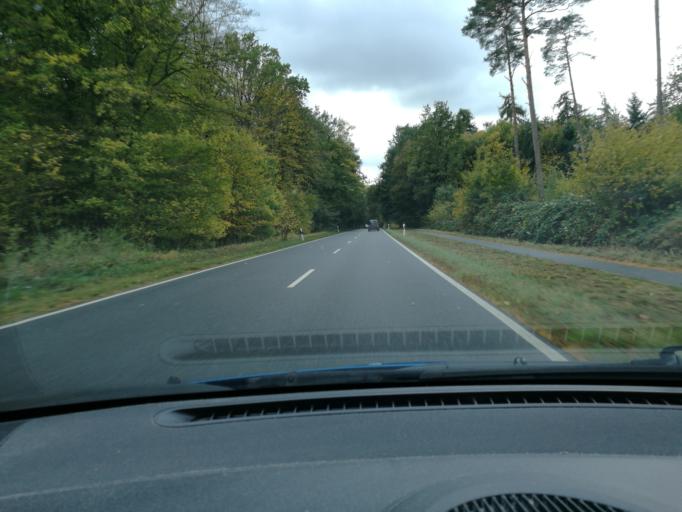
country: DE
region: Schleswig-Holstein
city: Gross Gronau
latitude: 53.7812
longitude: 10.7513
